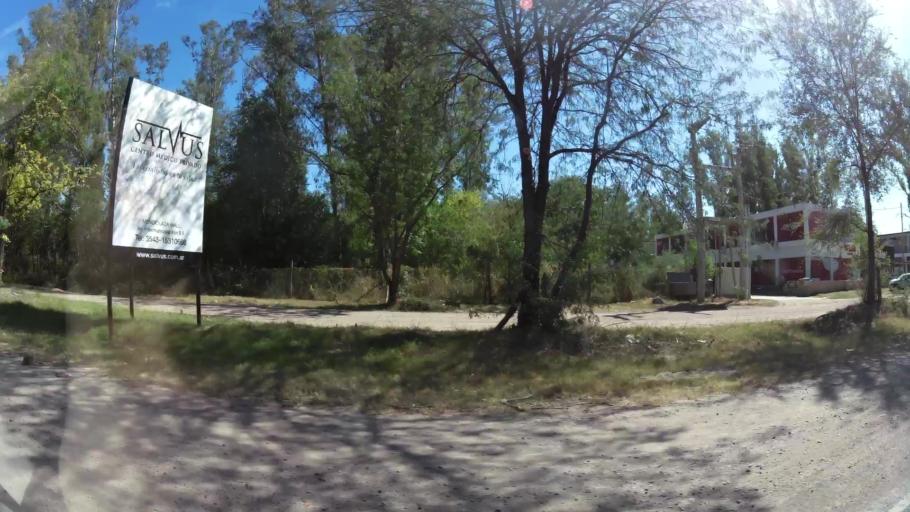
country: AR
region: Cordoba
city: Mendiolaza
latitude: -31.2701
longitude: -64.3017
